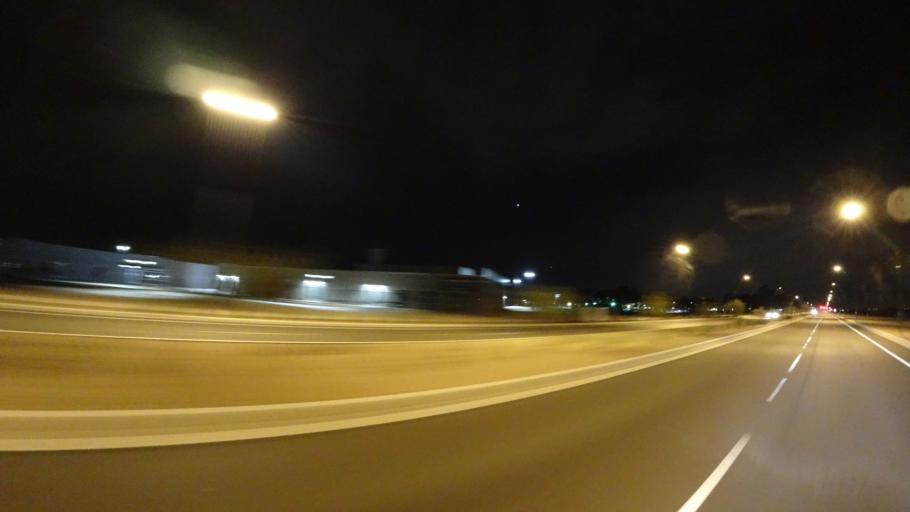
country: US
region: Arizona
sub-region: Maricopa County
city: Queen Creek
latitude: 33.2632
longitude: -111.6461
